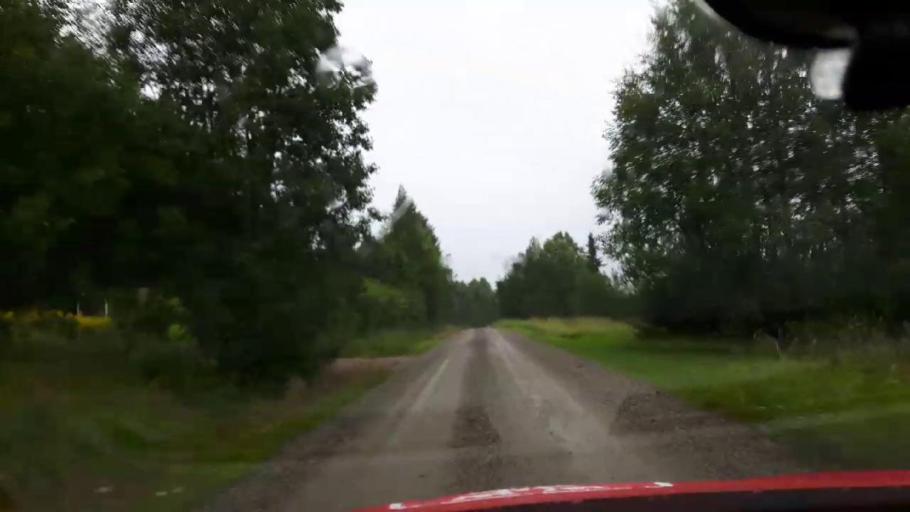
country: SE
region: Jaemtland
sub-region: OEstersunds Kommun
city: Brunflo
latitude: 62.7867
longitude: 14.9658
